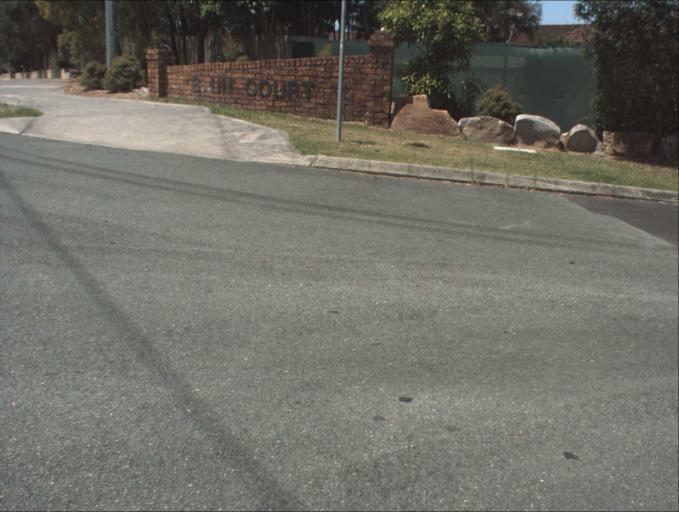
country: AU
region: Queensland
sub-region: Logan
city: Windaroo
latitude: -27.7466
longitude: 153.1921
